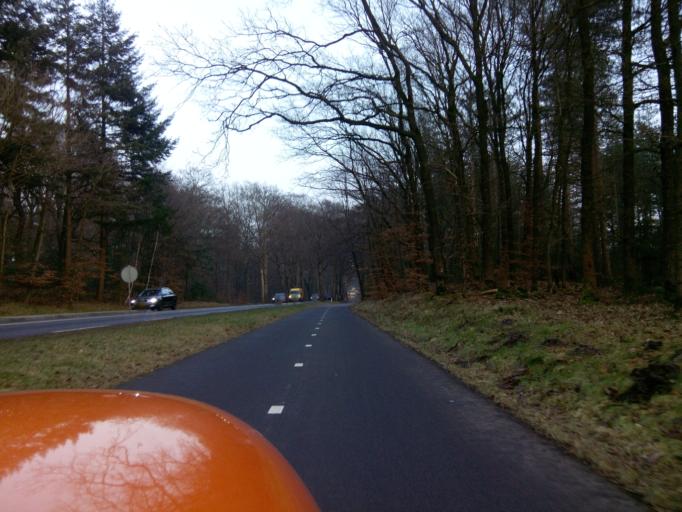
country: NL
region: Utrecht
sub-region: Gemeente Utrechtse Heuvelrug
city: Maarn
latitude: 52.0872
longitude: 5.3322
